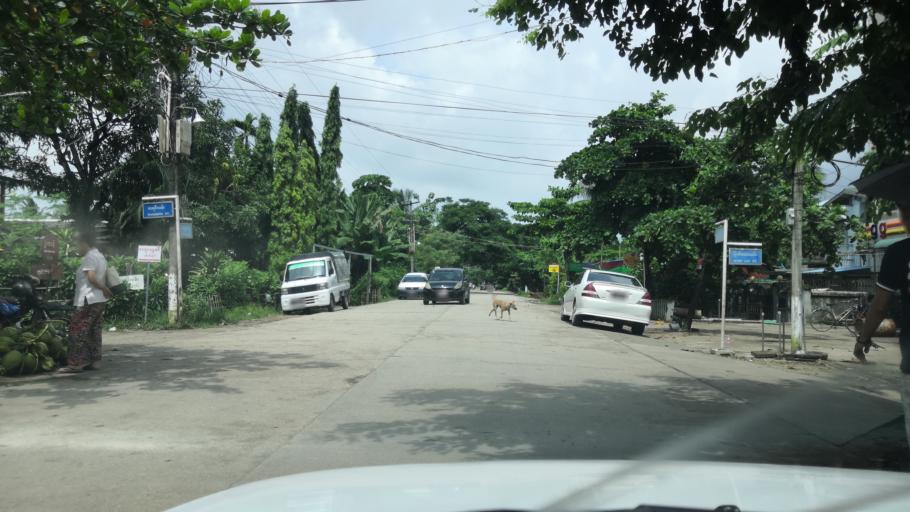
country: MM
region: Yangon
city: Yangon
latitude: 16.8750
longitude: 96.1823
